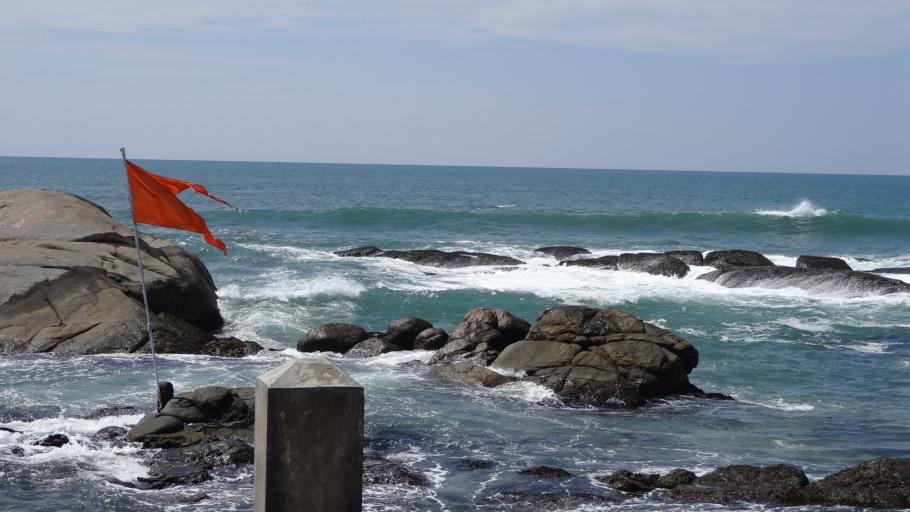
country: IN
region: Tamil Nadu
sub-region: Kanniyakumari
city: Kanniyakumari
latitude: 8.0781
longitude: 77.5510
